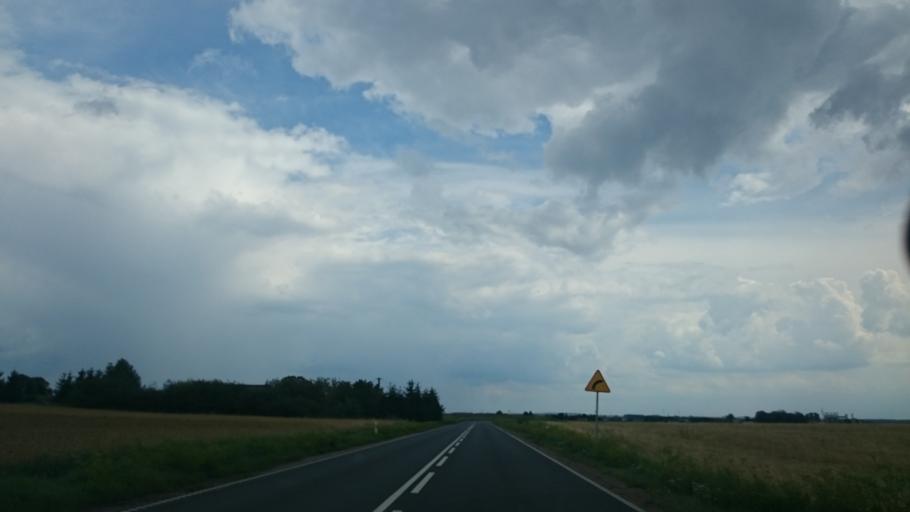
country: PL
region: Kujawsko-Pomorskie
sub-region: Powiat tucholski
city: Kesowo
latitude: 53.6613
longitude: 17.6788
